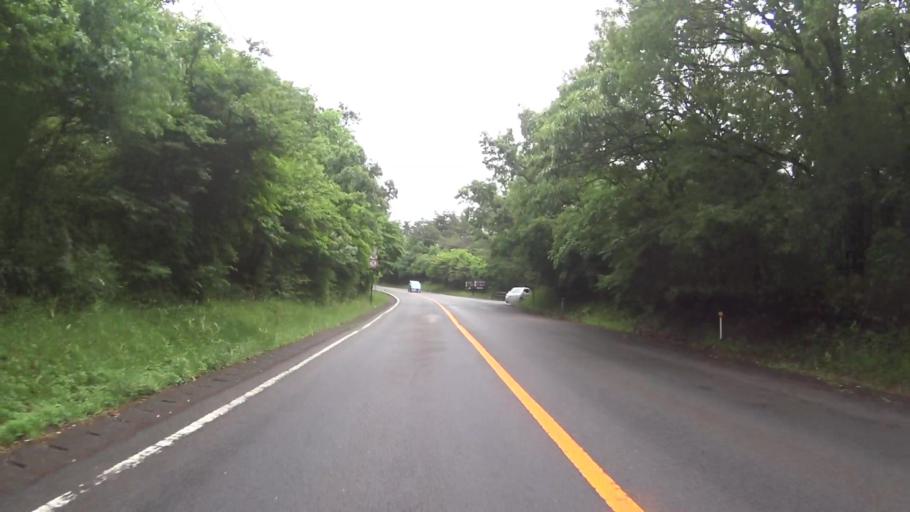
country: JP
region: Oita
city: Tsukawaki
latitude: 33.1154
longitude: 131.2276
